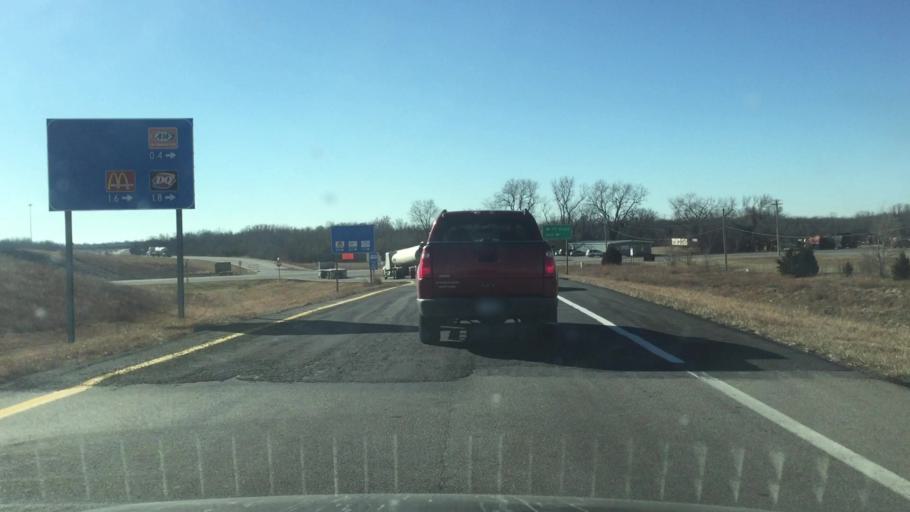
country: US
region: Kansas
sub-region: Allen County
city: Iola
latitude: 37.9237
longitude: -95.3801
